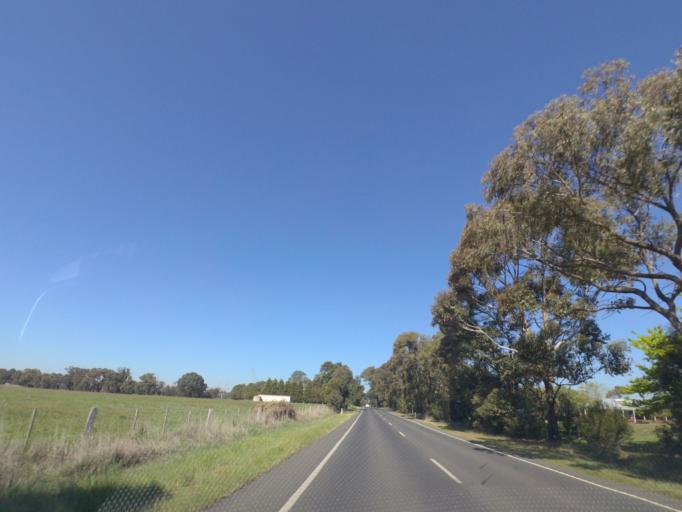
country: AU
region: Victoria
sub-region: Whittlesea
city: Whittlesea
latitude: -37.3262
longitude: 144.9671
